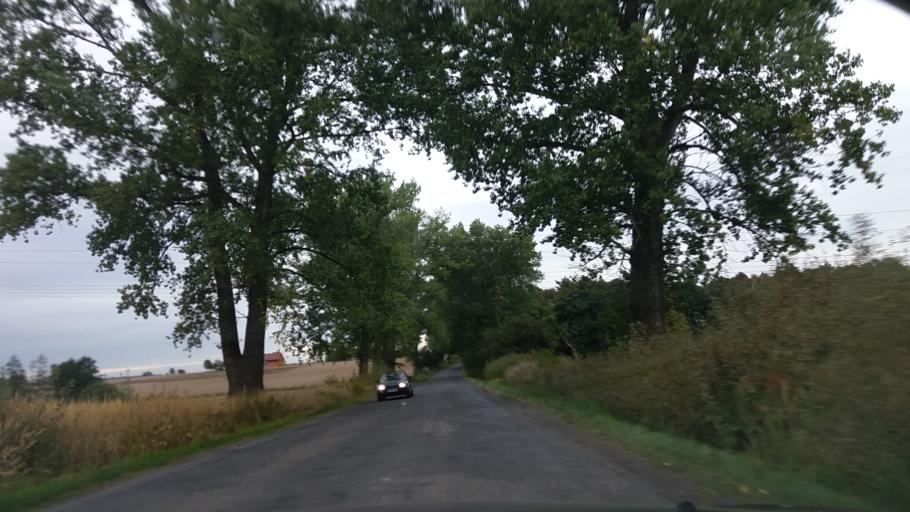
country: PL
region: Lower Silesian Voivodeship
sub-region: Powiat legnicki
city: Legnickie Pole
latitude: 51.1327
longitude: 16.3427
